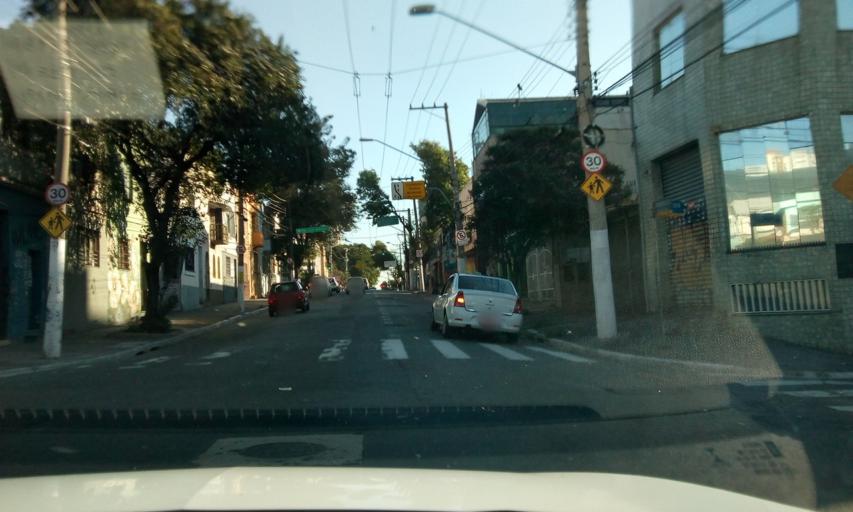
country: BR
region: Sao Paulo
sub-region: Guarulhos
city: Guarulhos
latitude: -23.5222
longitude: -46.5505
